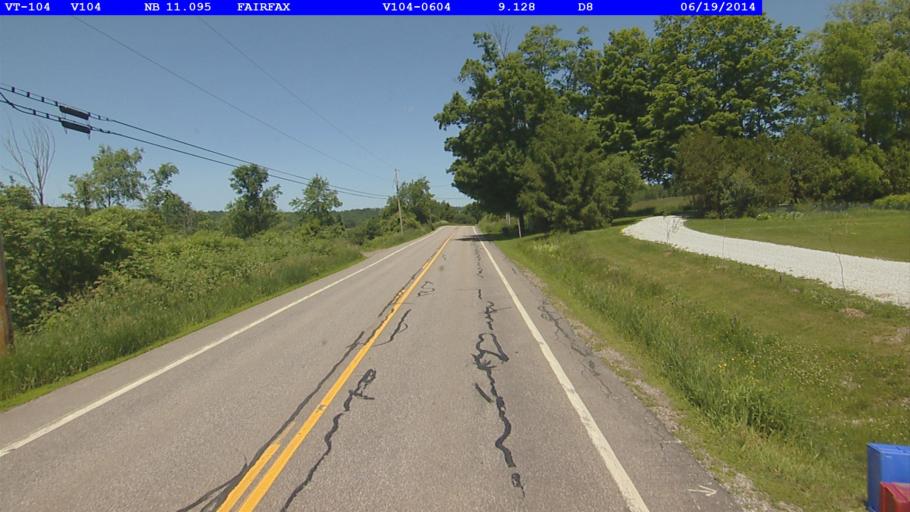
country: US
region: Vermont
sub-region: Chittenden County
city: Milton
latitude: 44.7158
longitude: -73.0407
